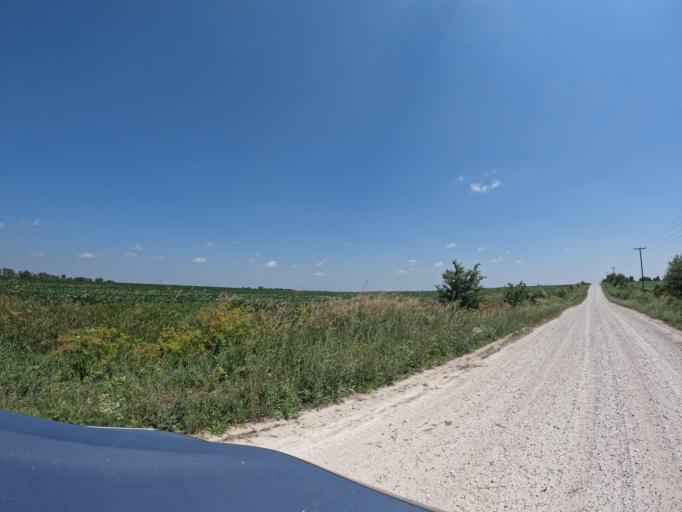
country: US
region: Iowa
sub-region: Keokuk County
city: Sigourney
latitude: 41.2795
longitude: -92.2378
